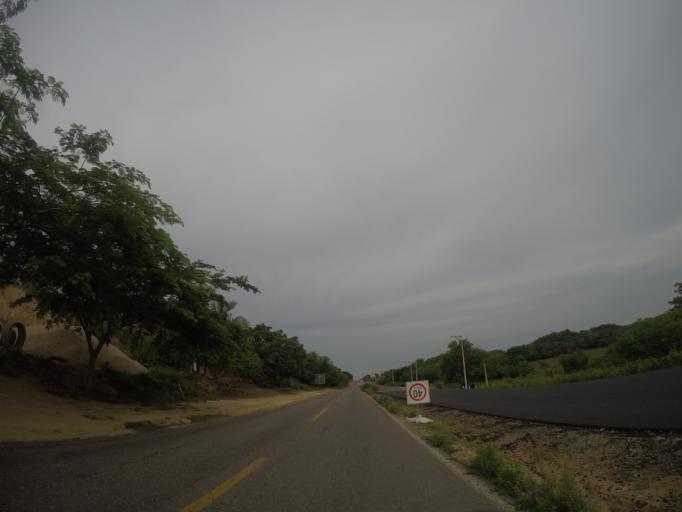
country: MX
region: Oaxaca
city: Santa Maria Tonameca
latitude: 15.7229
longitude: -96.6172
